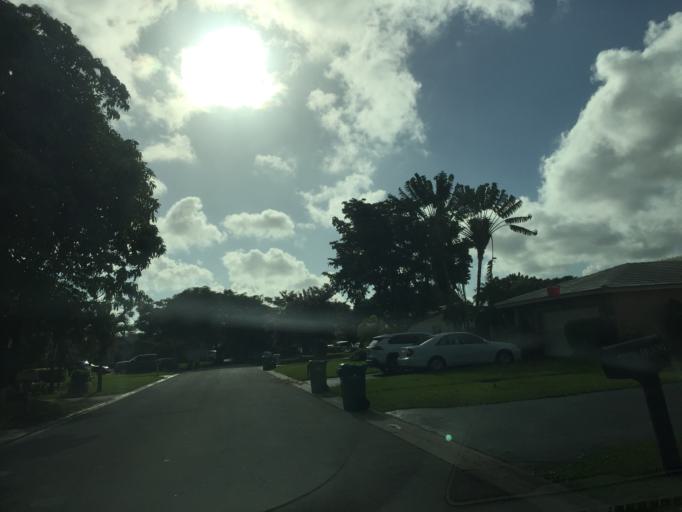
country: US
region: Florida
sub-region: Broward County
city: North Lauderdale
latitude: 26.2463
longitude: -80.2387
